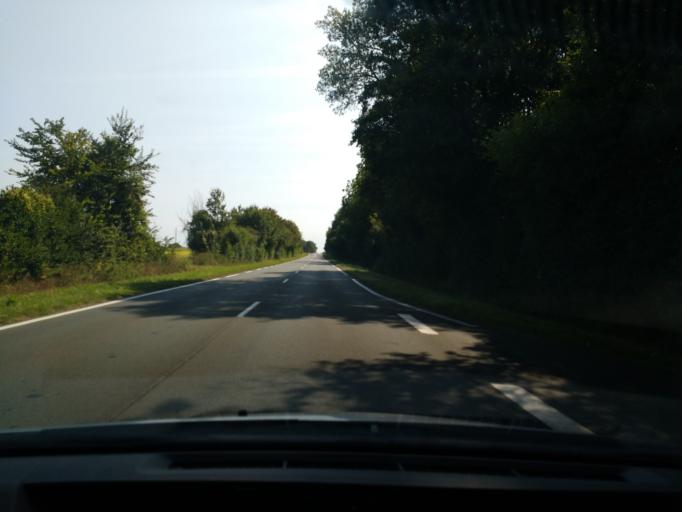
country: FR
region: Pays de la Loire
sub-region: Departement de Maine-et-Loire
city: Bauge-en-Anjou
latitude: 47.5313
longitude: -0.0503
